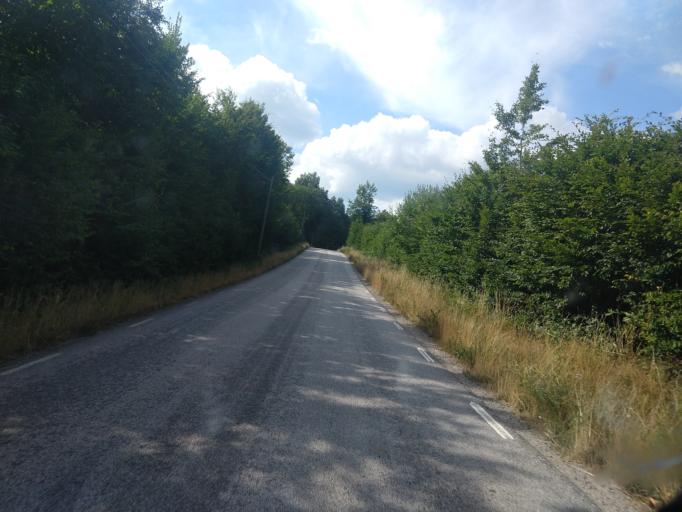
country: SE
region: Blekinge
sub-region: Karlskrona Kommun
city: Rodeby
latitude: 56.2334
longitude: 15.5787
